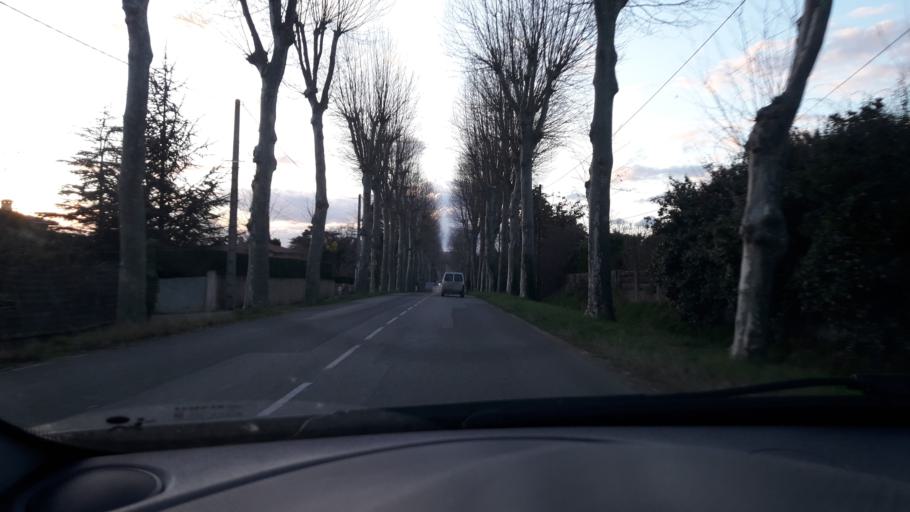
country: FR
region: Midi-Pyrenees
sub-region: Departement du Gers
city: Pujaudran
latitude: 43.6122
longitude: 1.0938
